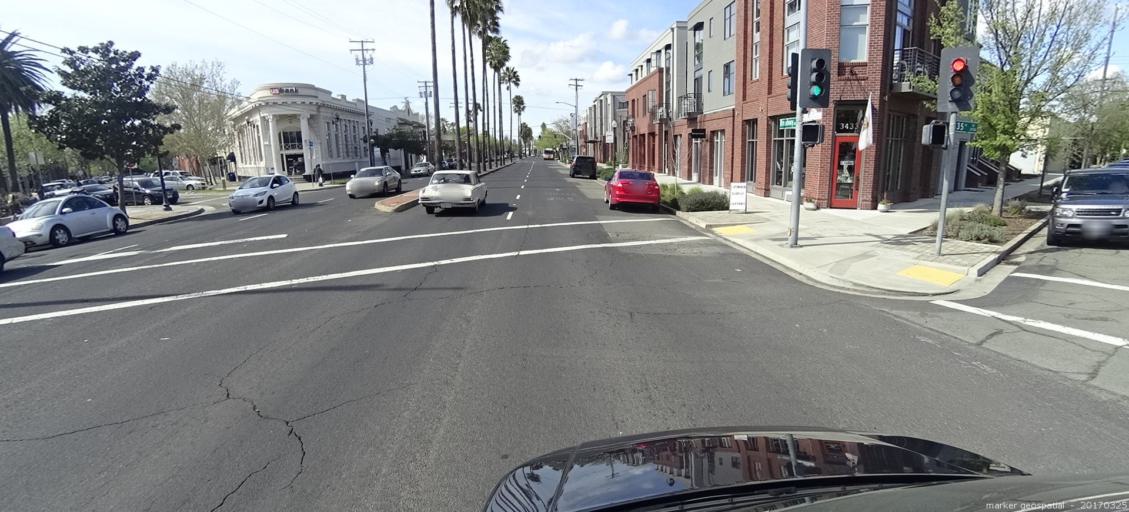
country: US
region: California
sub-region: Sacramento County
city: Sacramento
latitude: 38.5516
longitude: -121.4685
